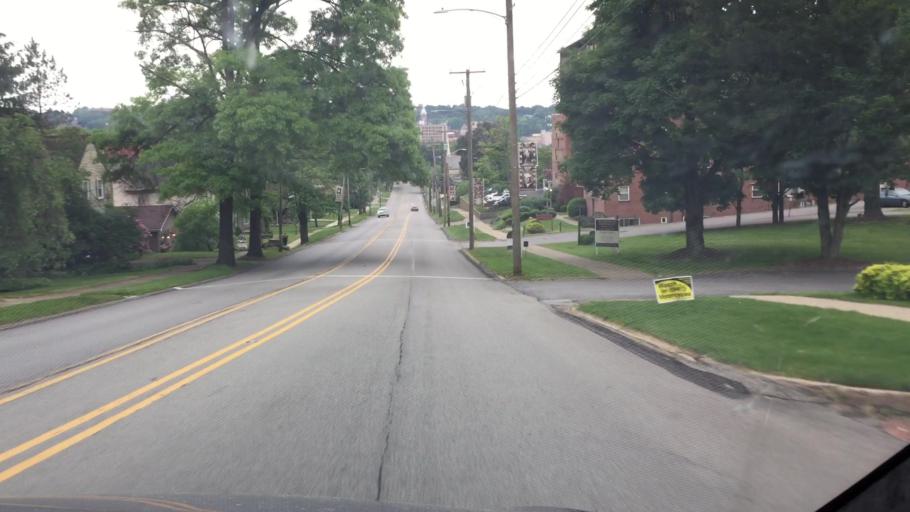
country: US
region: Pennsylvania
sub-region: Butler County
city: Butler
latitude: 40.8699
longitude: -79.8950
